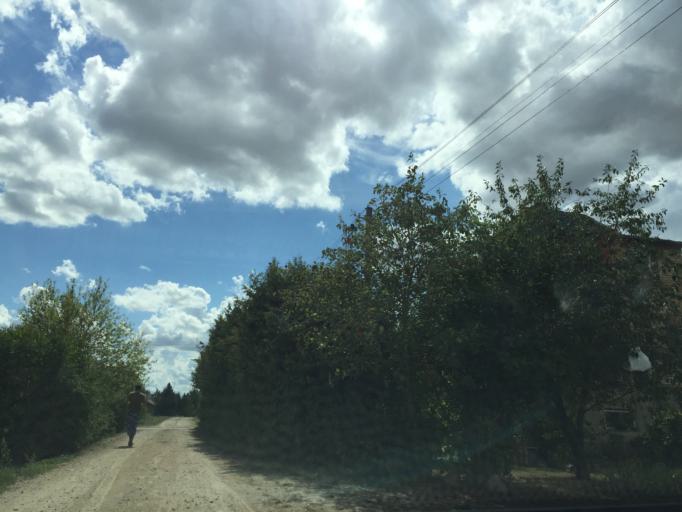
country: LT
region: Siauliu apskritis
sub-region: Joniskis
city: Joniskis
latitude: 56.2945
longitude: 23.8223
